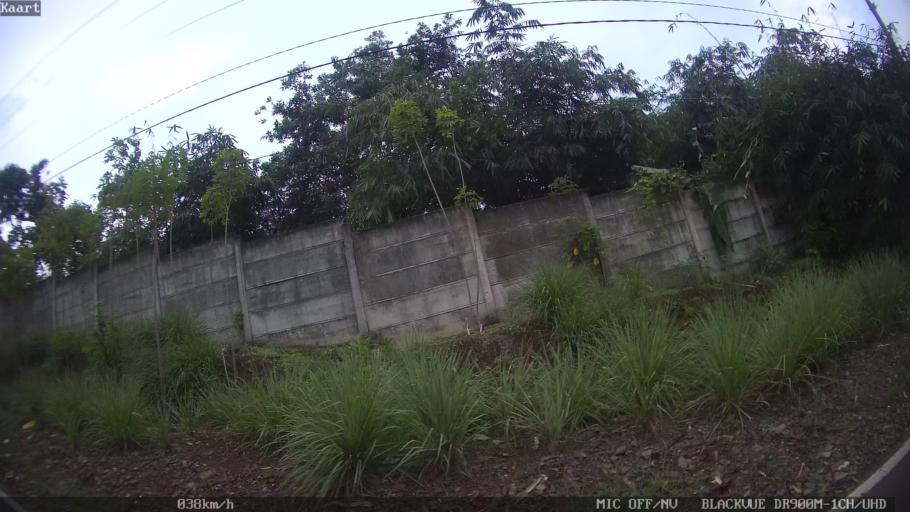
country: ID
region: Lampung
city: Bandarlampung
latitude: -5.4273
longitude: 105.1974
